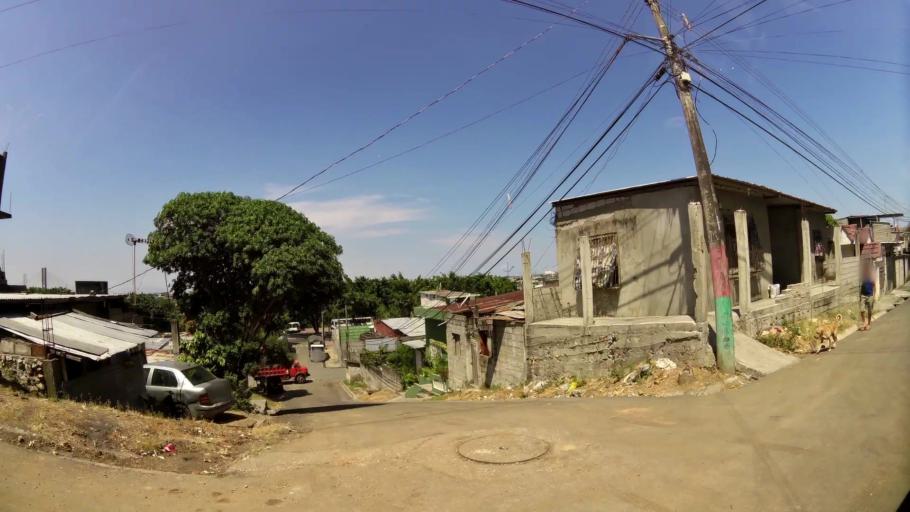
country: EC
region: Guayas
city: Guayaquil
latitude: -2.1876
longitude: -79.9296
